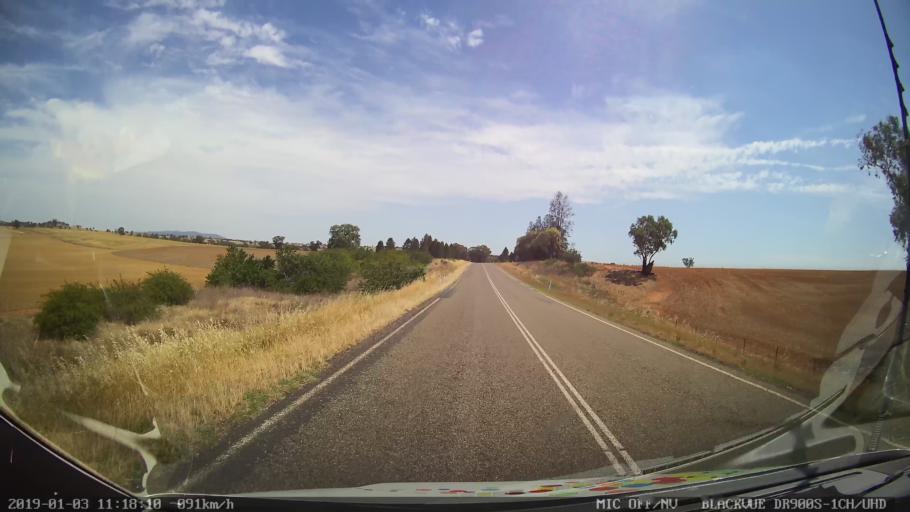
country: AU
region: New South Wales
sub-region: Young
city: Young
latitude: -34.1294
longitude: 148.2637
